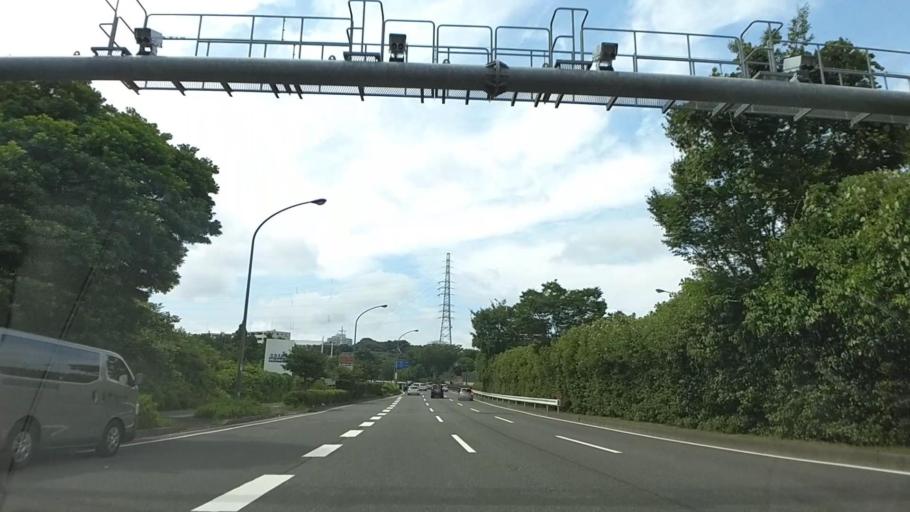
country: JP
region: Kanagawa
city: Yokohama
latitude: 35.4401
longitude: 139.5604
